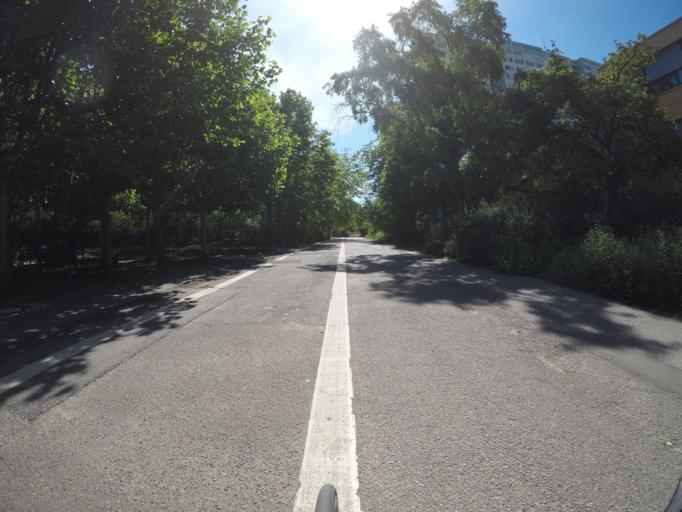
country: DE
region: Berlin
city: Prenzlauer Berg Bezirk
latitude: 52.5418
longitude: 13.4467
